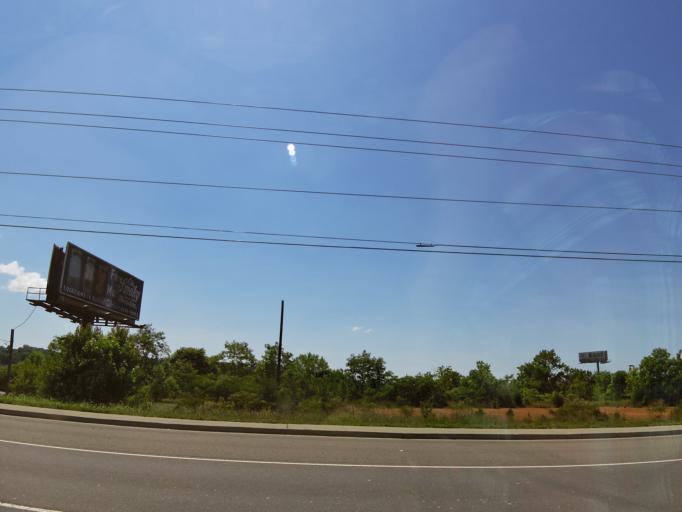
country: US
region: Tennessee
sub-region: Sevier County
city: Sevierville
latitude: 35.9268
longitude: -83.5827
